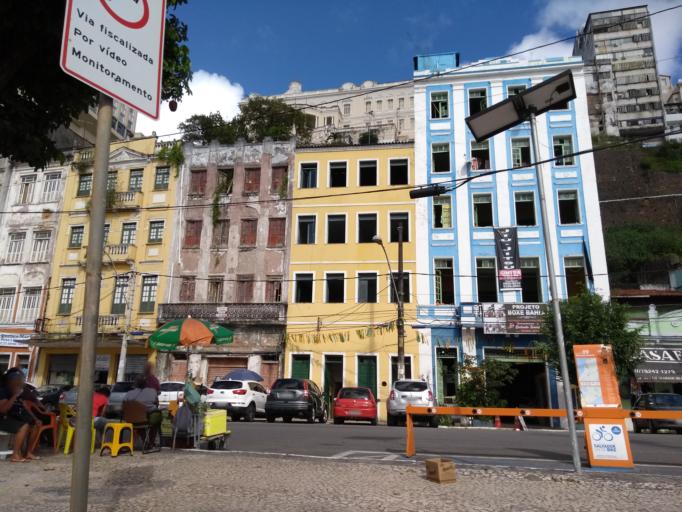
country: BR
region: Bahia
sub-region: Salvador
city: Salvador
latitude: -12.9745
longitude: -38.5141
